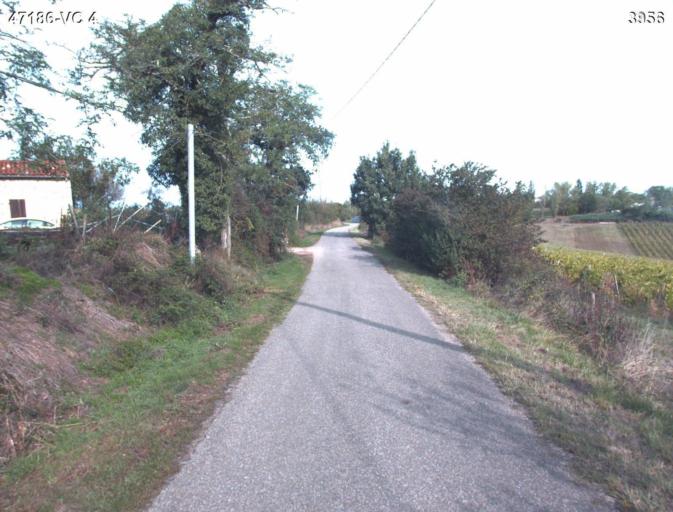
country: FR
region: Aquitaine
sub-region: Departement du Lot-et-Garonne
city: Sainte-Colombe-en-Bruilhois
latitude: 44.1963
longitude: 0.4469
